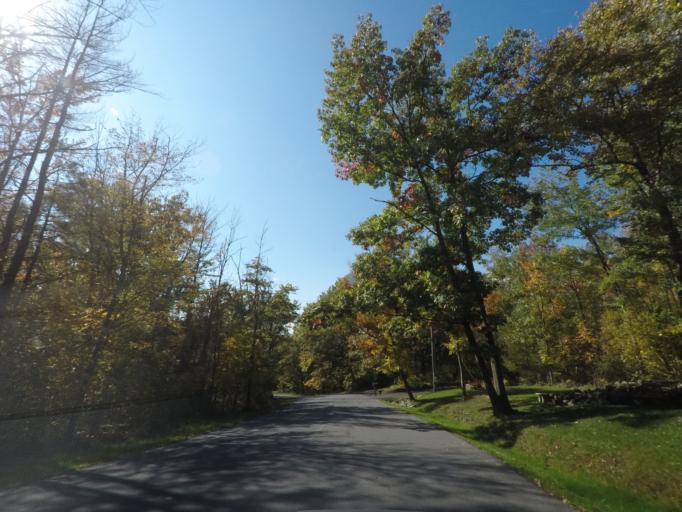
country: US
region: New York
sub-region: Rensselaer County
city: Averill Park
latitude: 42.6452
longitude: -73.5565
